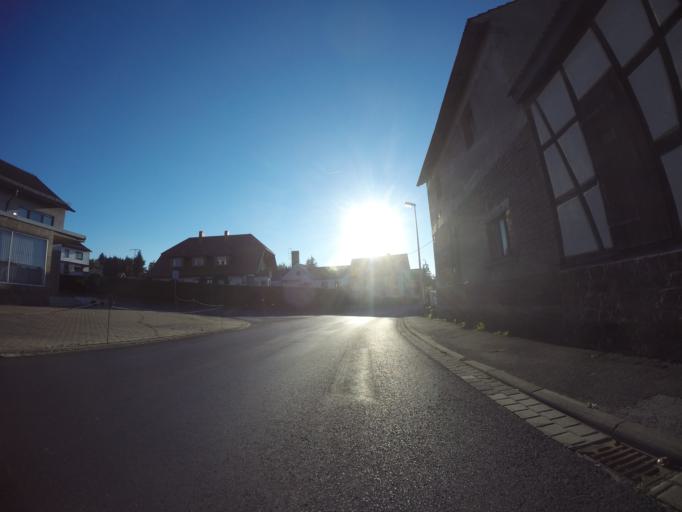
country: DE
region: Bavaria
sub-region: Regierungsbezirk Unterfranken
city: Schollbrunn
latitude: 49.8348
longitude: 9.4642
